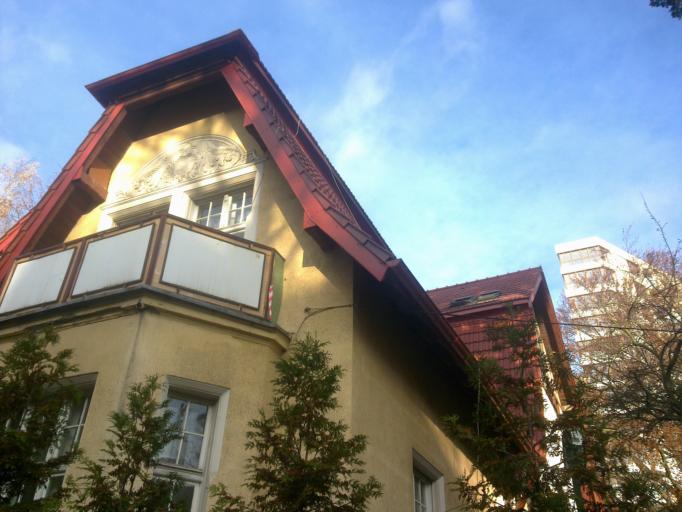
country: PL
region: Pomeranian Voivodeship
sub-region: Gdansk
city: Gdansk
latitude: 54.3760
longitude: 18.6037
